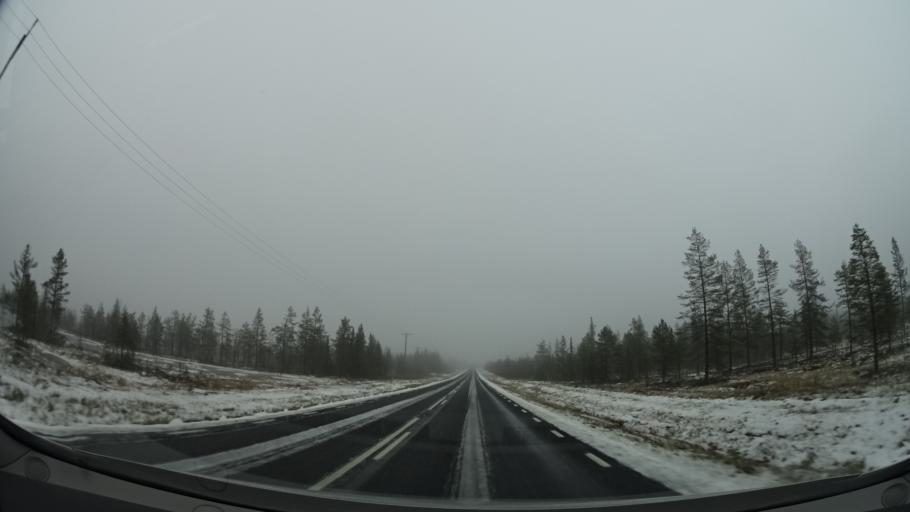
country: SE
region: Vaesterbotten
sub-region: Lycksele Kommun
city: Soderfors
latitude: 64.4127
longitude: 18.0233
